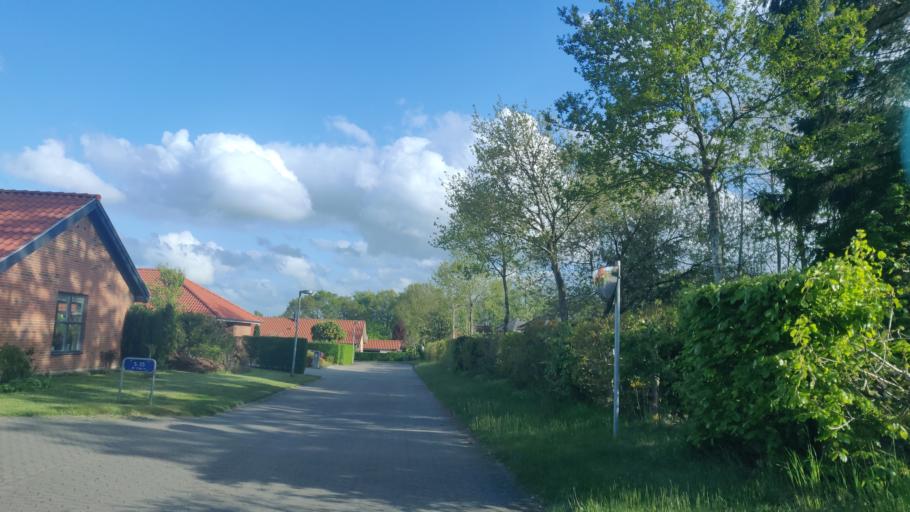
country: DK
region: Central Jutland
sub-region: Viborg Kommune
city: Bjerringbro
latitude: 56.3799
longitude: 9.6453
